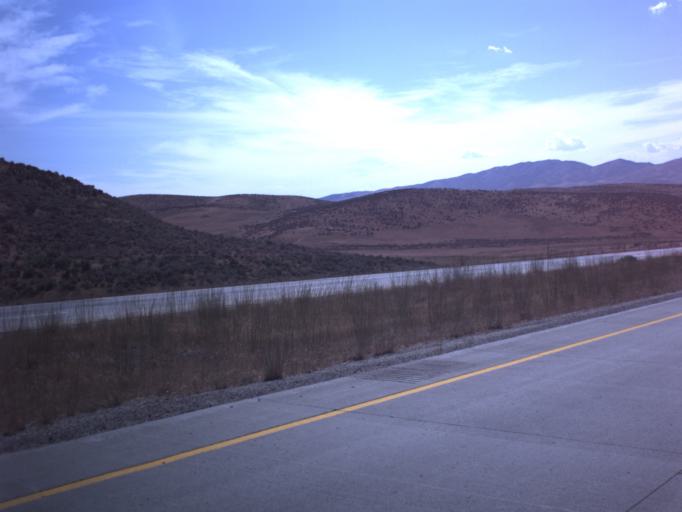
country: US
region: Utah
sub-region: Box Elder County
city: Garland
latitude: 41.8158
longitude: -112.3640
